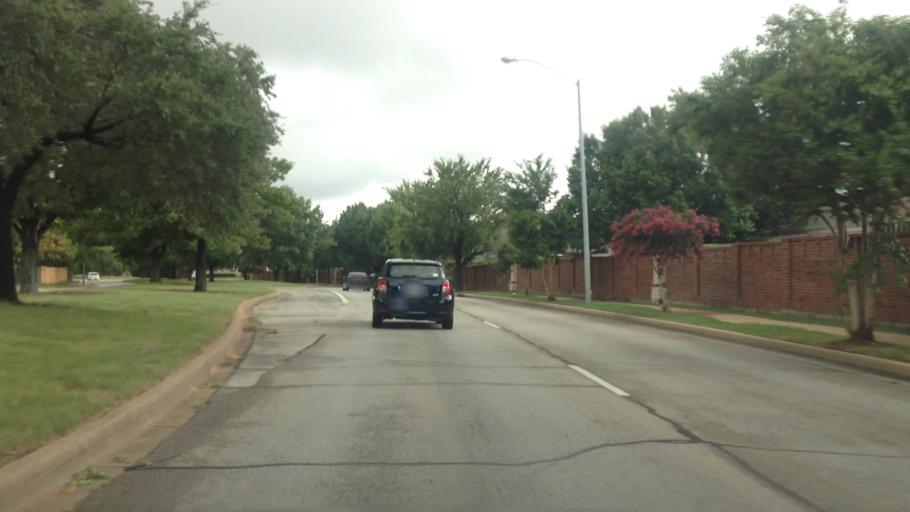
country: US
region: Texas
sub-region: Tarrant County
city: Edgecliff Village
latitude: 32.6395
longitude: -97.3959
